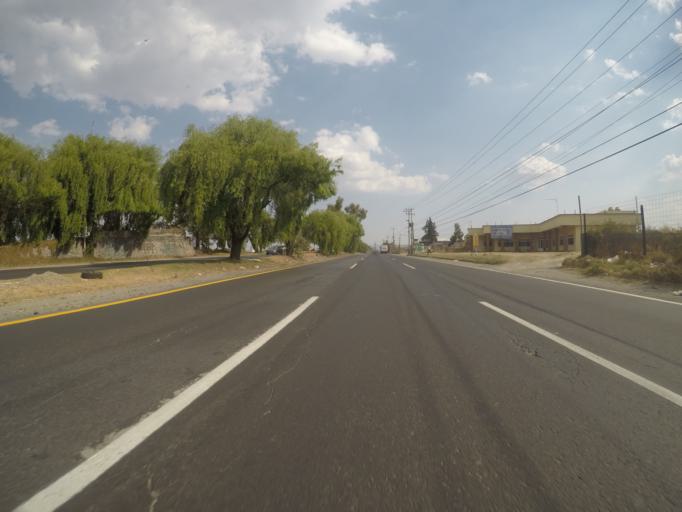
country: MX
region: Morelos
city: San Miguel Totocuitlapilco
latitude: 19.2231
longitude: -99.5934
